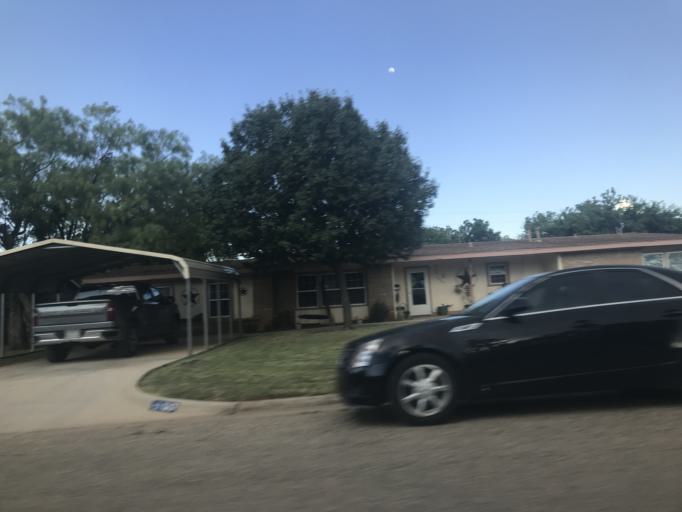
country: US
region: Texas
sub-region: Taylor County
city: Abilene
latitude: 32.4290
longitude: -99.7670
